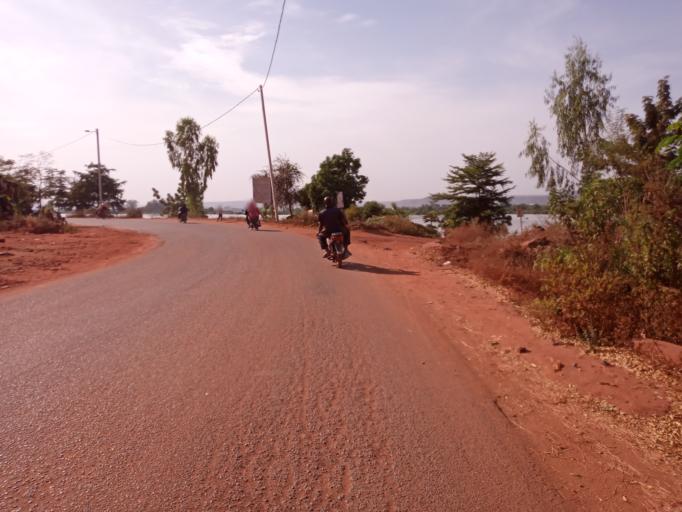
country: ML
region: Bamako
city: Bamako
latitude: 12.6298
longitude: -7.9516
